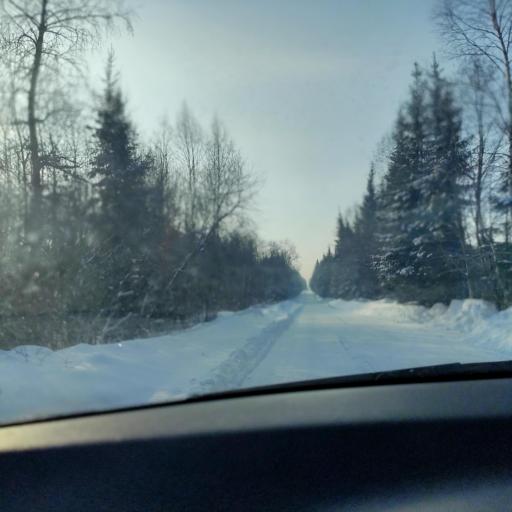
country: RU
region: Perm
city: Kondratovo
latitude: 58.0764
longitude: 56.1296
